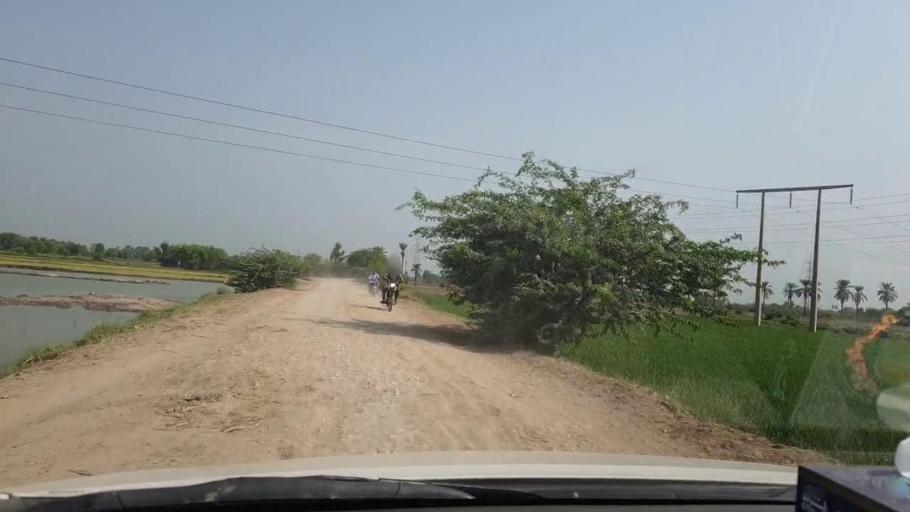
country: PK
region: Sindh
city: Shikarpur
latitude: 27.9716
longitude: 68.6653
